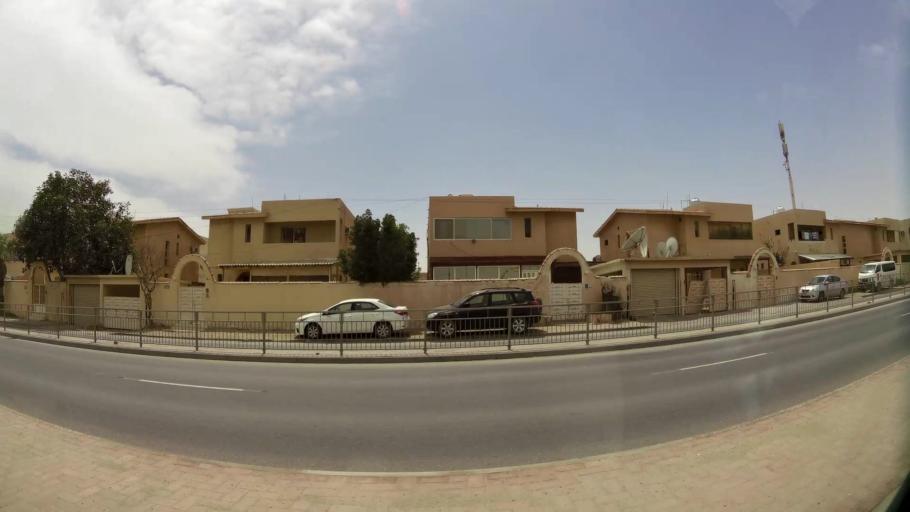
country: QA
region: Baladiyat ar Rayyan
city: Ar Rayyan
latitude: 25.2860
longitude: 51.4259
